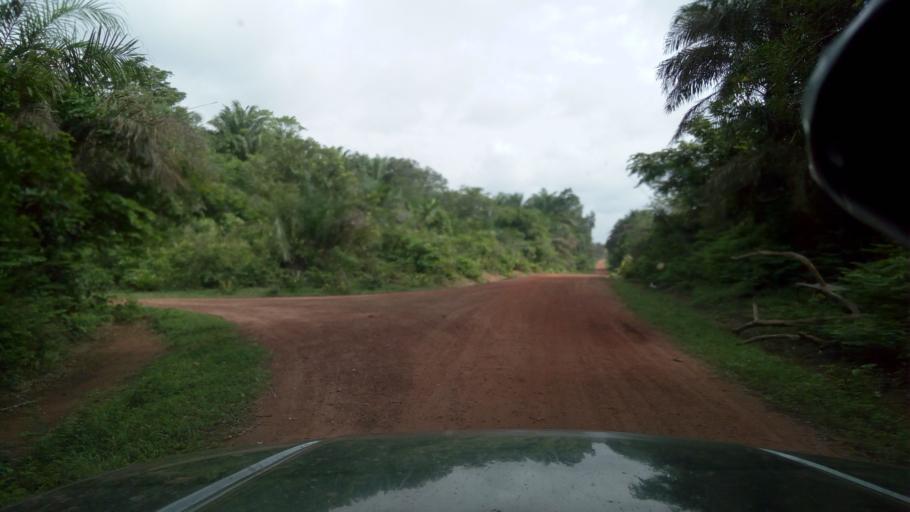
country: SL
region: Northern Province
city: Mange
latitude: 8.8127
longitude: -12.9305
